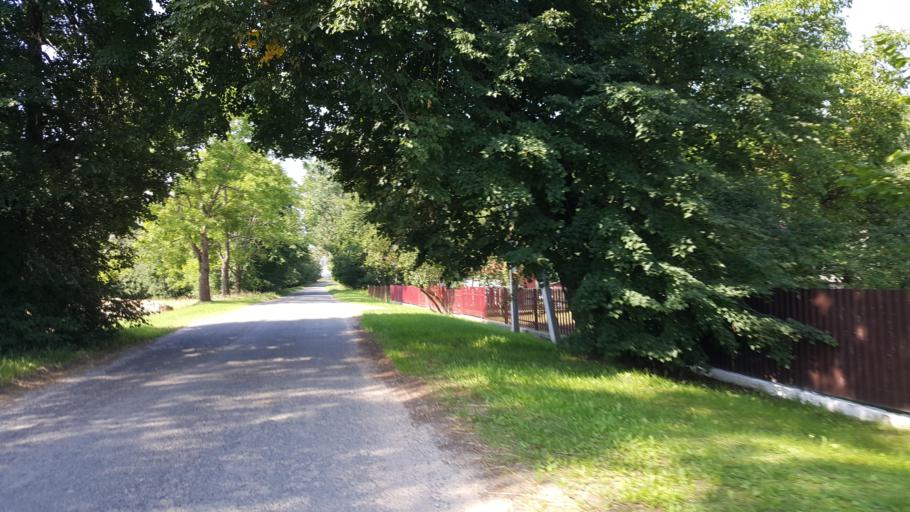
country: BY
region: Brest
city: Zhabinka
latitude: 52.2371
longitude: 24.0052
